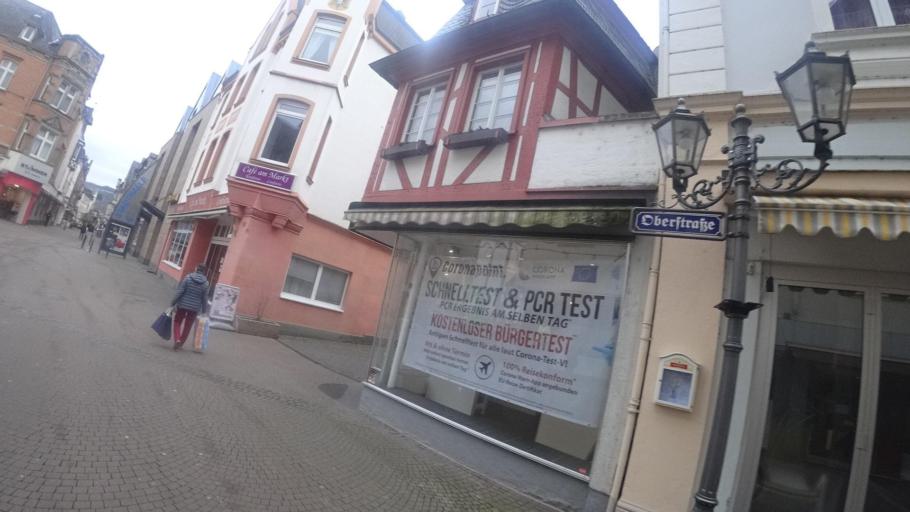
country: DE
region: Rheinland-Pfalz
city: Boppard
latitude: 50.2317
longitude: 7.5909
